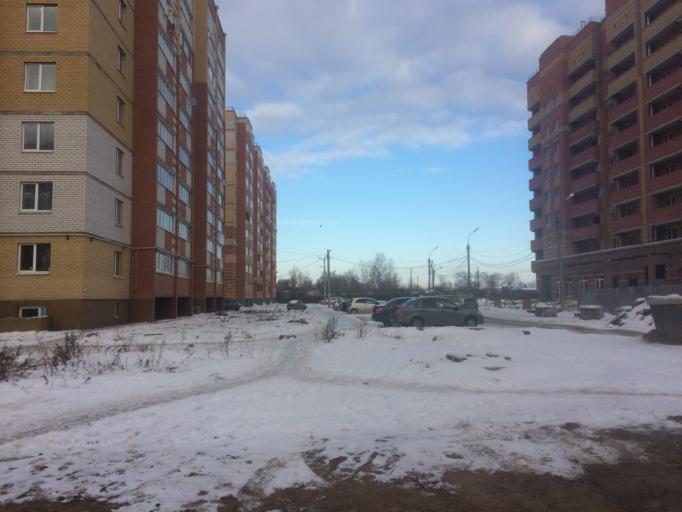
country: RU
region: Mariy-El
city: Yoshkar-Ola
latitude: 56.6386
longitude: 47.9287
